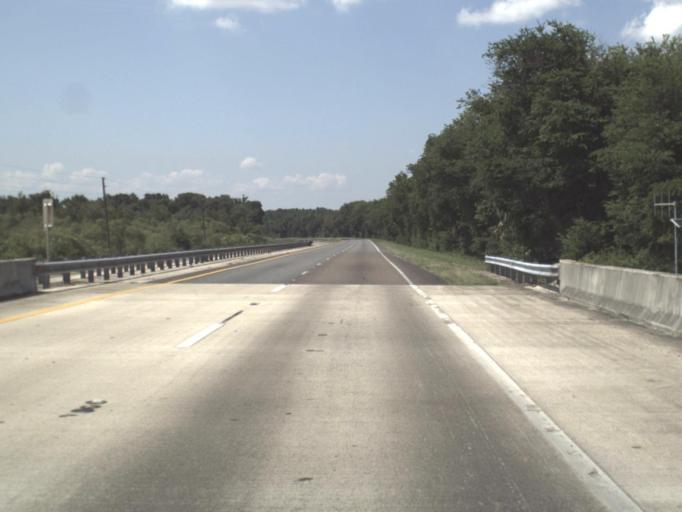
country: US
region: Florida
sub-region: Marion County
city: Citra
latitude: 29.4417
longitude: -82.1088
